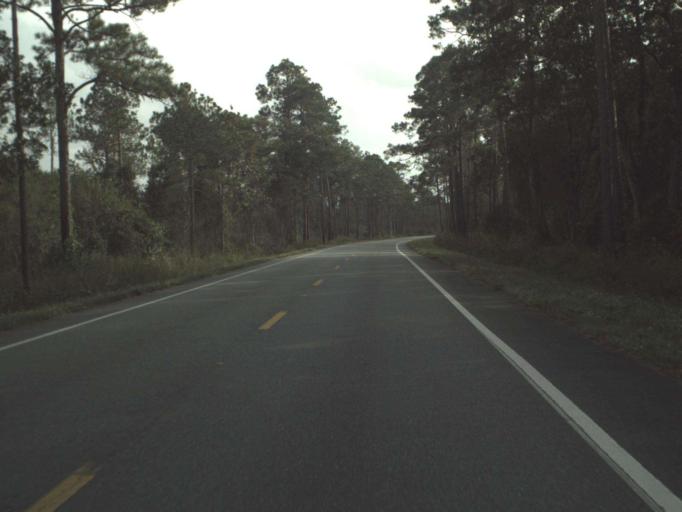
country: US
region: Florida
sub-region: Franklin County
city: Apalachicola
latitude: 29.9771
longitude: -84.9751
